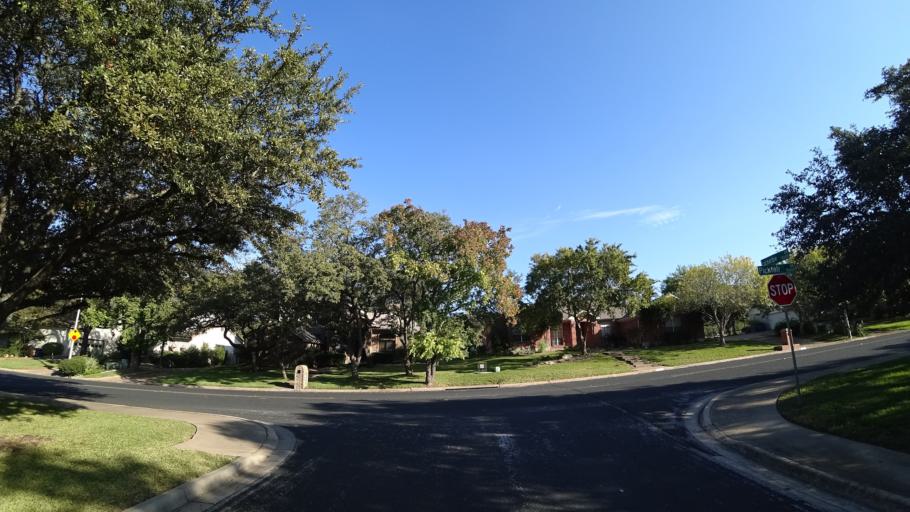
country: US
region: Texas
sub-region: Williamson County
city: Anderson Mill
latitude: 30.4337
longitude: -97.8105
